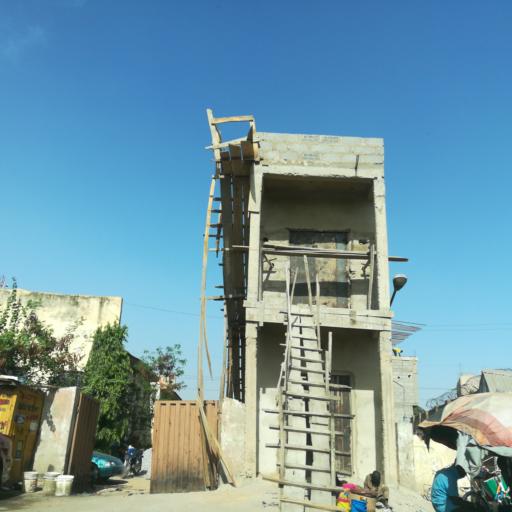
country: NG
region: Kano
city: Kano
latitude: 12.0101
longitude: 8.5232
